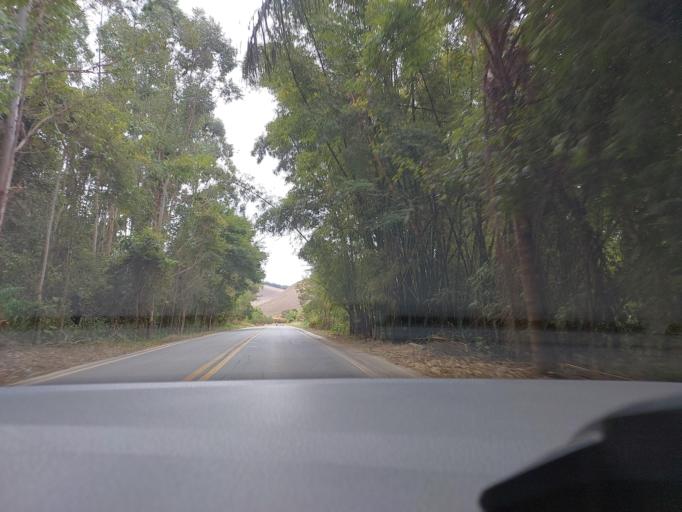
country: BR
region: Minas Gerais
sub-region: Vicosa
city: Vicosa
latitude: -20.8271
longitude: -42.7366
